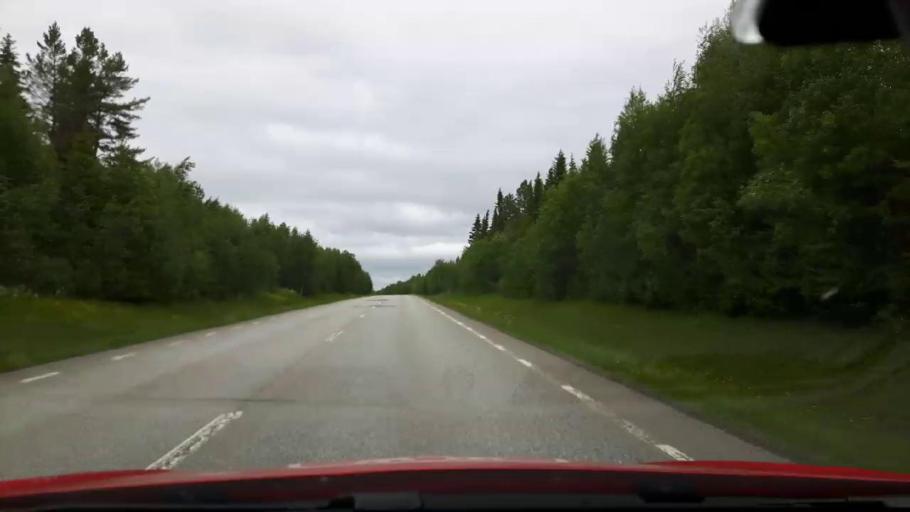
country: SE
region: Jaemtland
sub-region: OEstersunds Kommun
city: Lit
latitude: 63.6156
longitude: 14.6751
